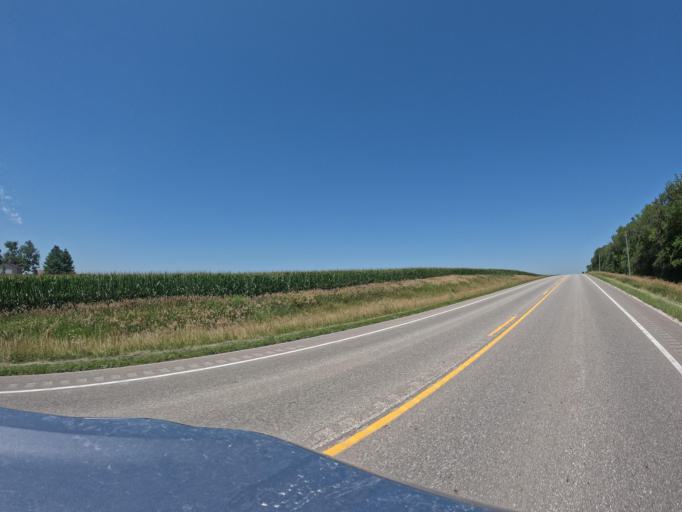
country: US
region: Iowa
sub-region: Keokuk County
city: Sigourney
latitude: 41.4677
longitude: -92.3552
